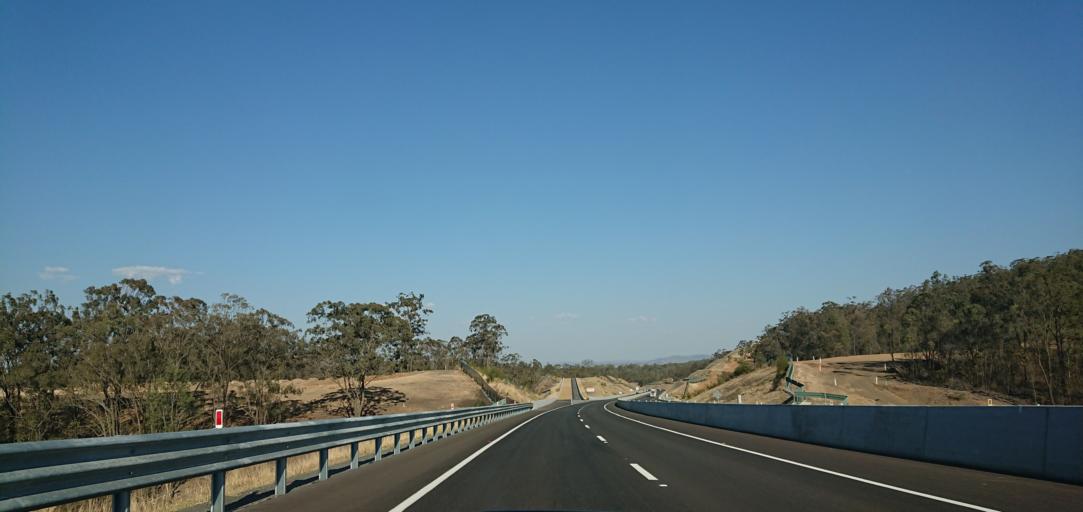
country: AU
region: Queensland
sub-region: Toowoomba
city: East Toowoomba
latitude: -27.5088
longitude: 152.0132
